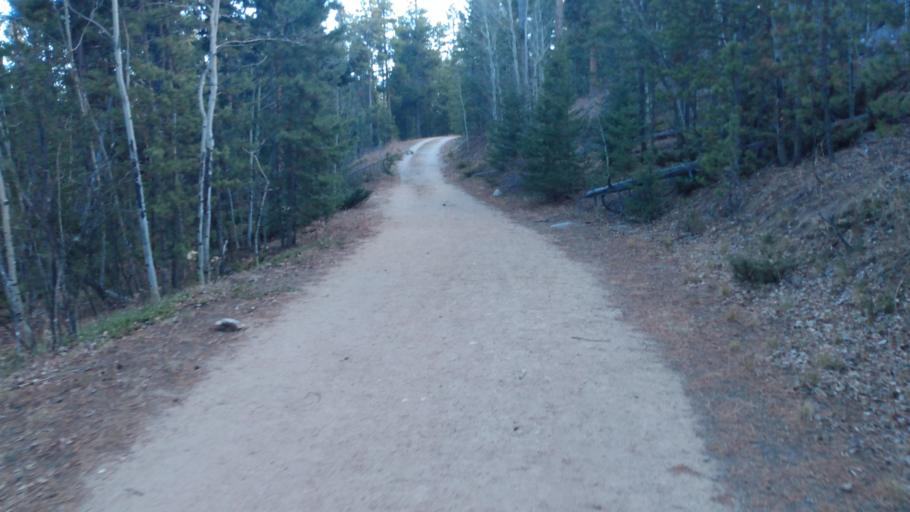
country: US
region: Colorado
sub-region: Boulder County
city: Nederland
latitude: 39.9614
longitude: -105.4486
